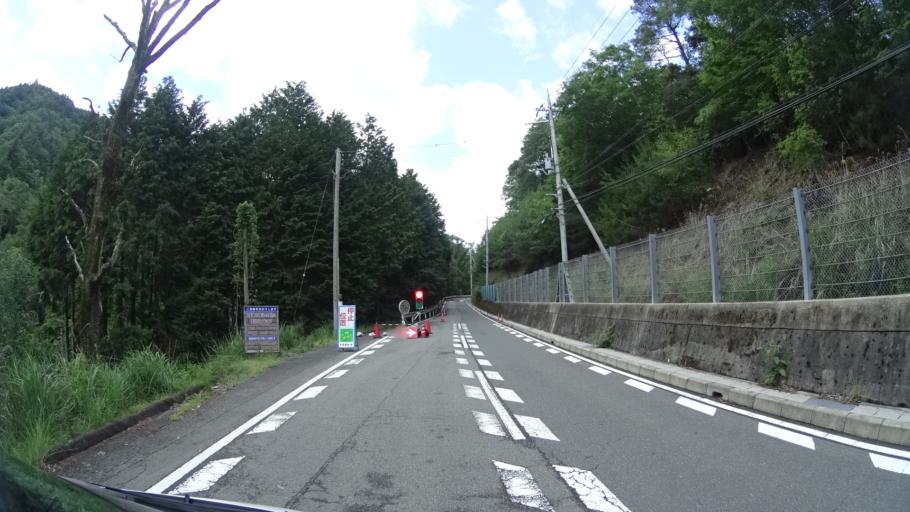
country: JP
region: Kyoto
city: Kameoka
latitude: 35.0180
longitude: 135.4109
